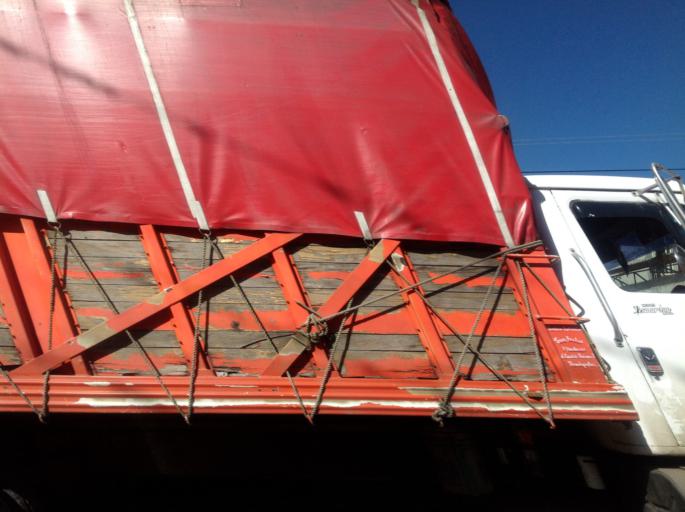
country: MX
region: Oaxaca
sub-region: Heroica Ciudad de Huajuapan de Leon
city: La Junta
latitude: 17.8179
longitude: -97.7602
